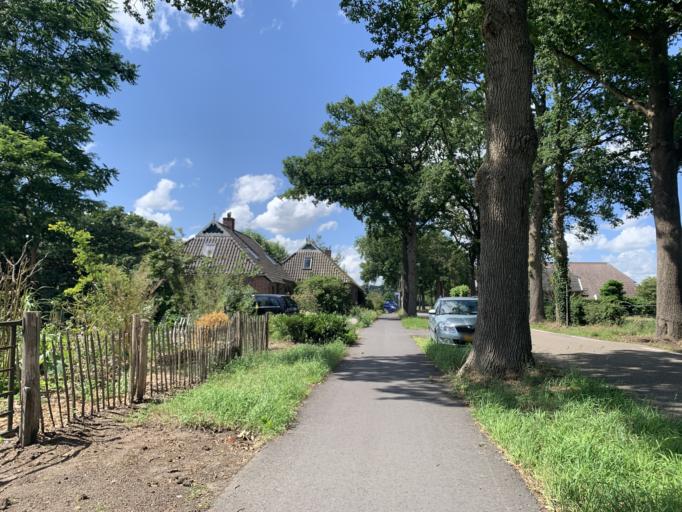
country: NL
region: Drenthe
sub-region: Gemeente Tynaarlo
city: Zuidlaren
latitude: 53.1325
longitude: 6.6584
